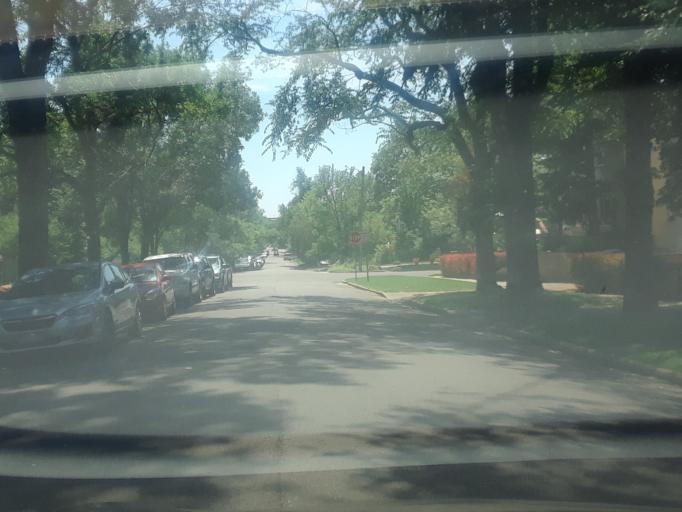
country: US
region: Colorado
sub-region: Arapahoe County
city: Glendale
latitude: 39.7248
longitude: -104.9534
